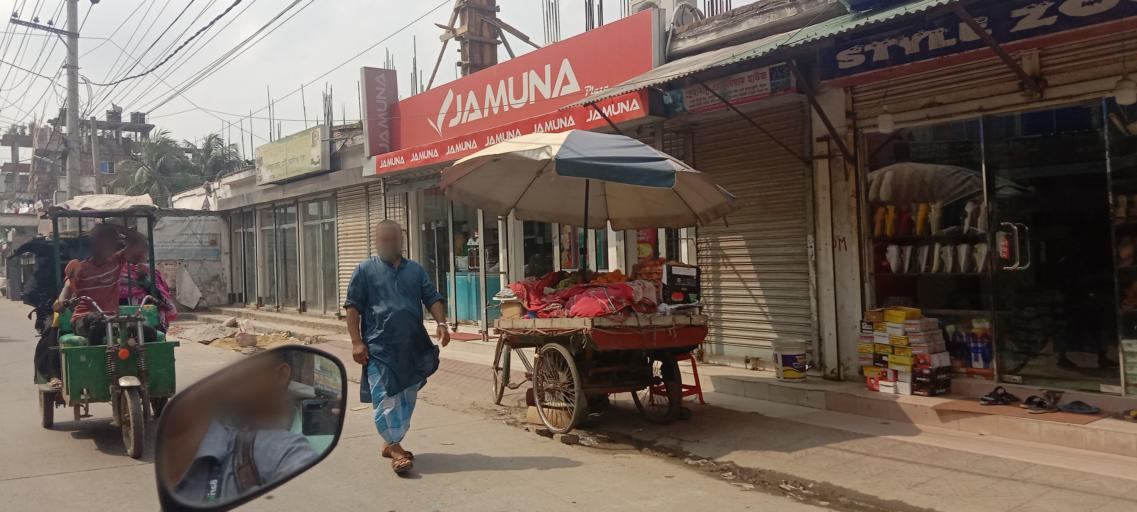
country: BD
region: Dhaka
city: Azimpur
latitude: 23.7141
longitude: 90.3572
